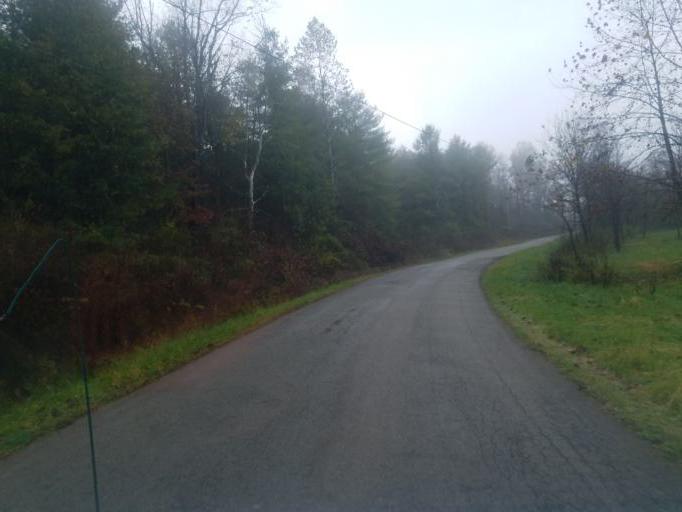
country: US
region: Ohio
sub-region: Athens County
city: Glouster
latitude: 39.4533
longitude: -81.9265
